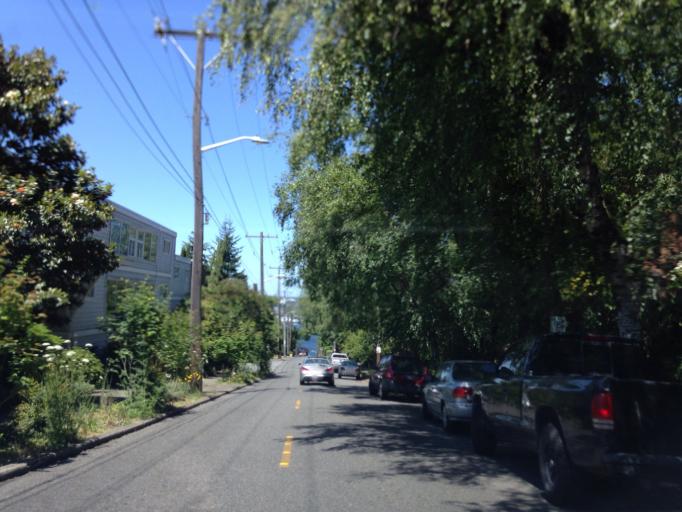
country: US
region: Washington
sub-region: King County
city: Seattle
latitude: 47.6257
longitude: -122.3246
